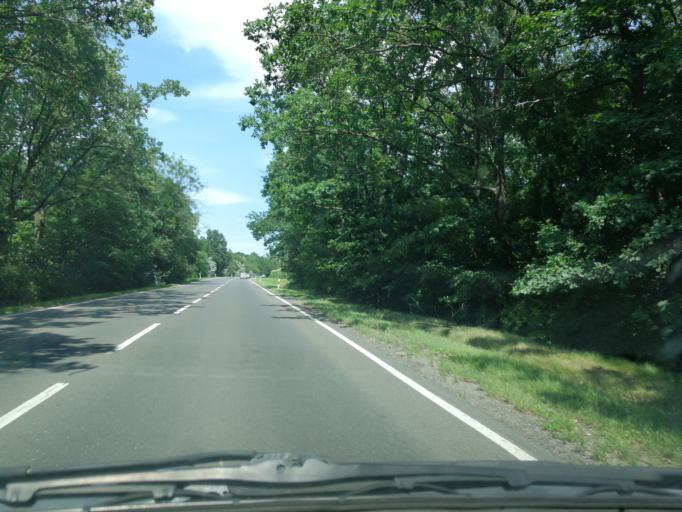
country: HU
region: Baranya
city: Hosszuheteny
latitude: 46.1276
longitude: 18.3701
